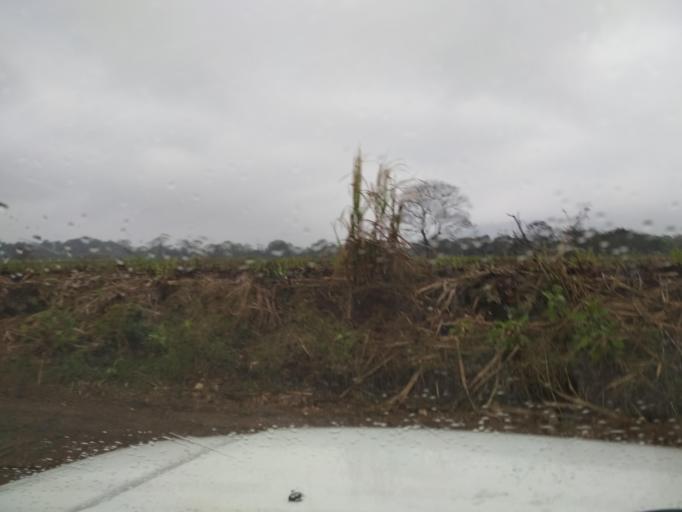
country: MX
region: Veracruz
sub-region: Cordoba
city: Veinte de Noviembre
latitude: 18.8580
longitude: -96.9631
